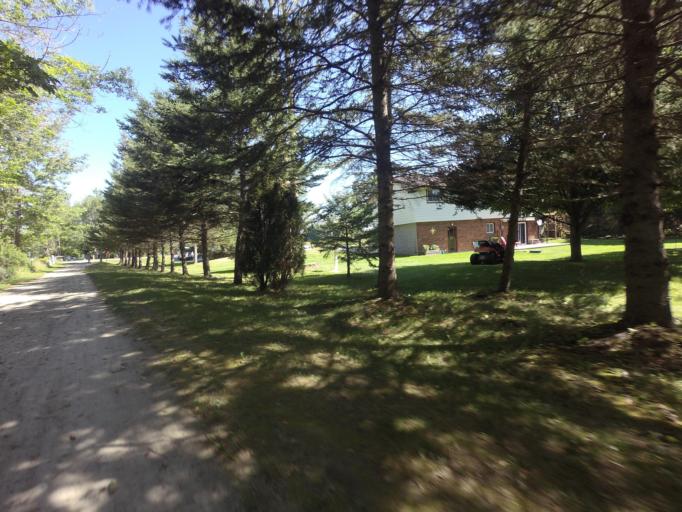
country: CA
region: Ontario
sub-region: Wellington County
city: Guelph
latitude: 43.7261
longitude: -80.3709
